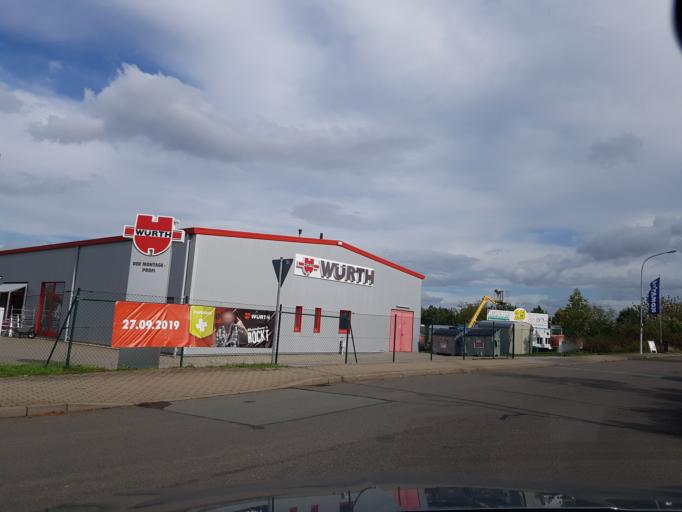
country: DE
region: Saxony
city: Riesa
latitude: 51.2956
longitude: 13.2861
